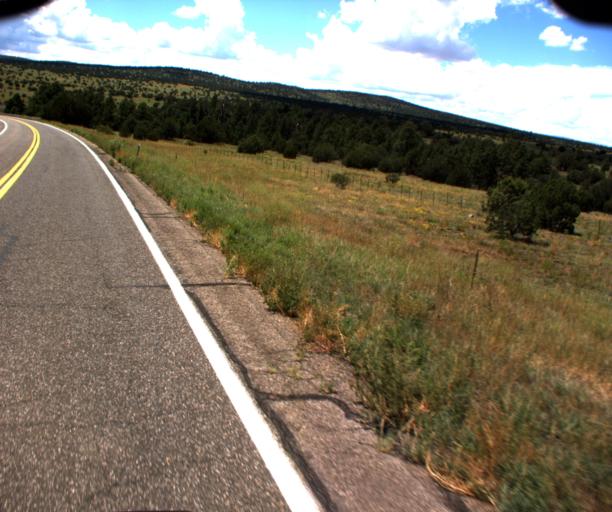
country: US
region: Arizona
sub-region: Gila County
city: Pine
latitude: 34.5053
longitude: -111.5728
